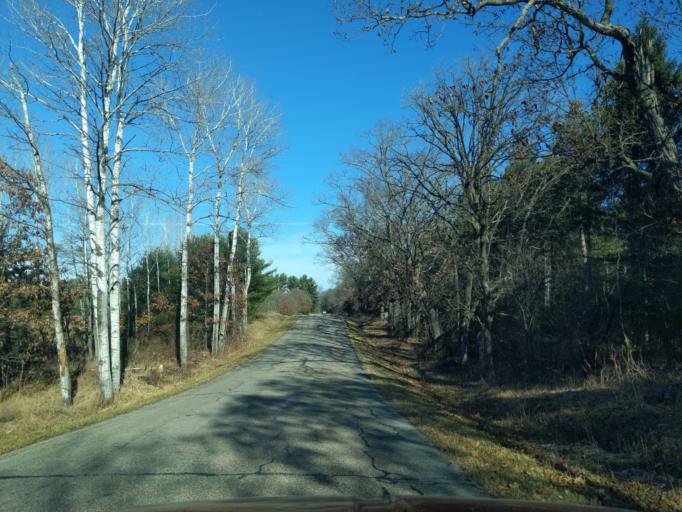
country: US
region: Wisconsin
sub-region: Waushara County
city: Silver Lake
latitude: 44.0730
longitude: -89.1938
